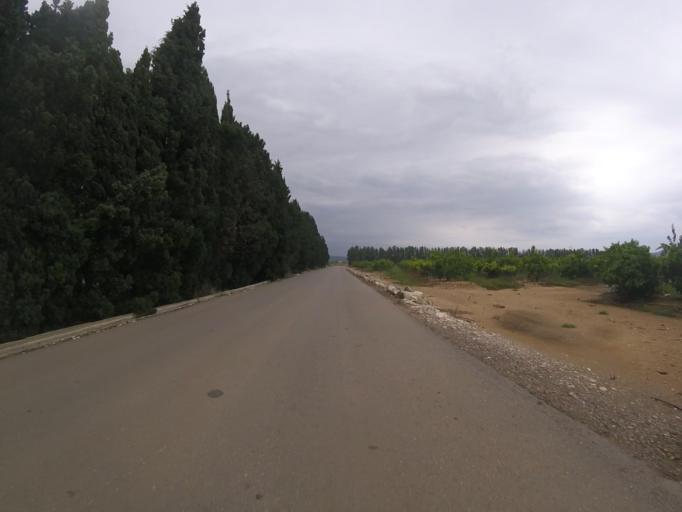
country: ES
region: Valencia
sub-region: Provincia de Castello
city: Alcoceber
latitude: 40.2103
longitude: 0.2515
